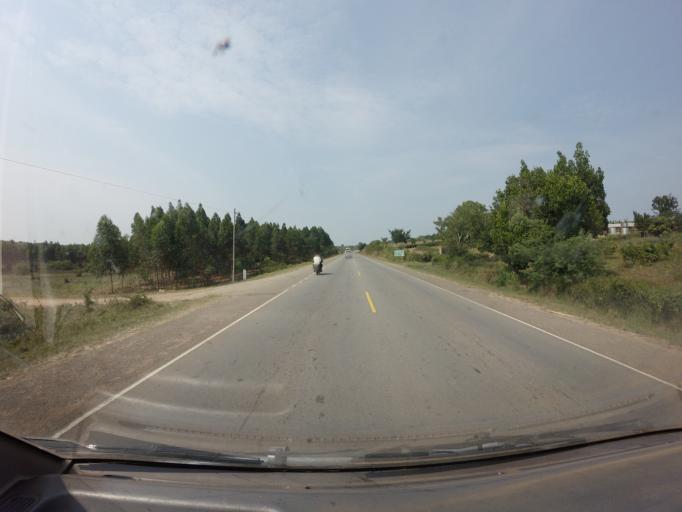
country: UG
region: Central Region
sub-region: Lwengo District
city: Lwengo
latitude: -0.4003
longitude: 31.3943
